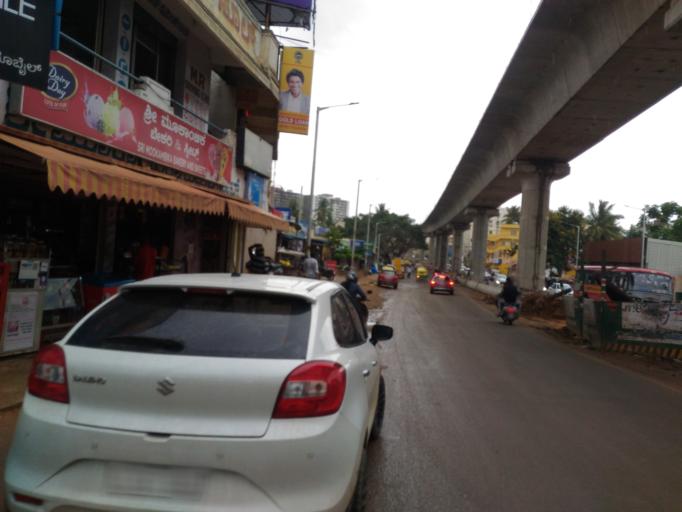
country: IN
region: Karnataka
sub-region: Bangalore Urban
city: Bangalore
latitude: 12.8746
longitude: 77.5415
